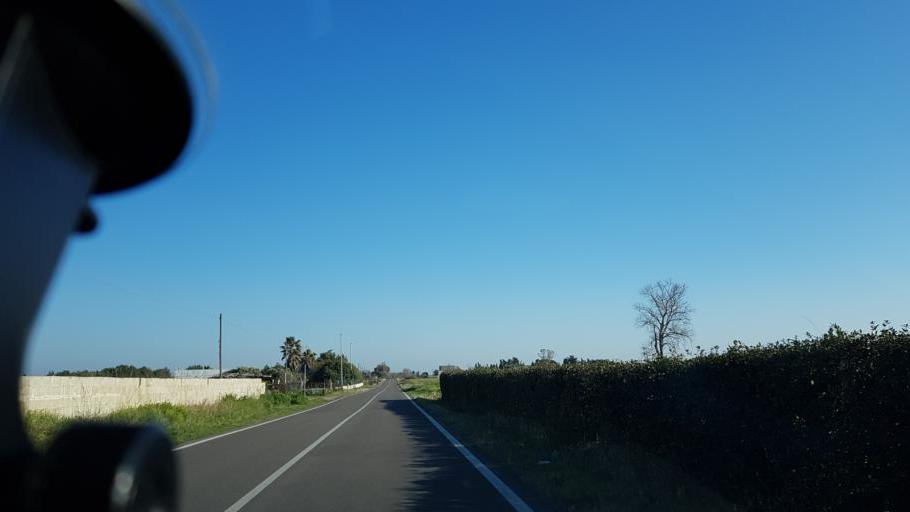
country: IT
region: Apulia
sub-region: Provincia di Lecce
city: Merine
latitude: 40.4173
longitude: 18.2510
